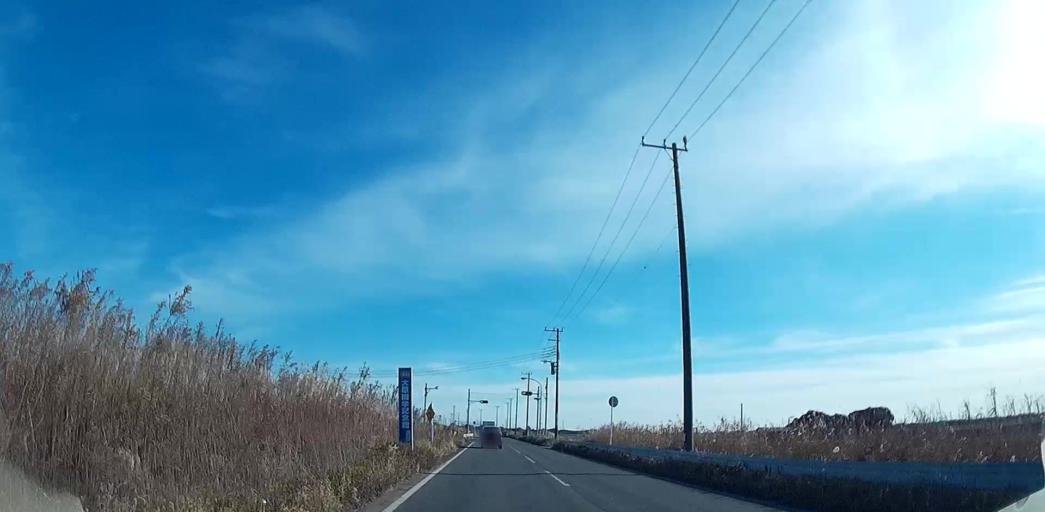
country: JP
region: Chiba
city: Yokaichiba
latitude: 35.7425
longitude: 140.5772
